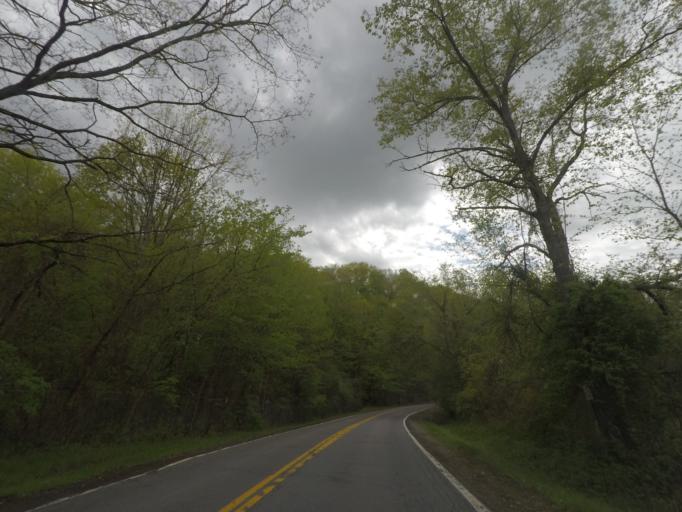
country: US
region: New York
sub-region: Albany County
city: Voorheesville
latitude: 42.6901
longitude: -73.9219
